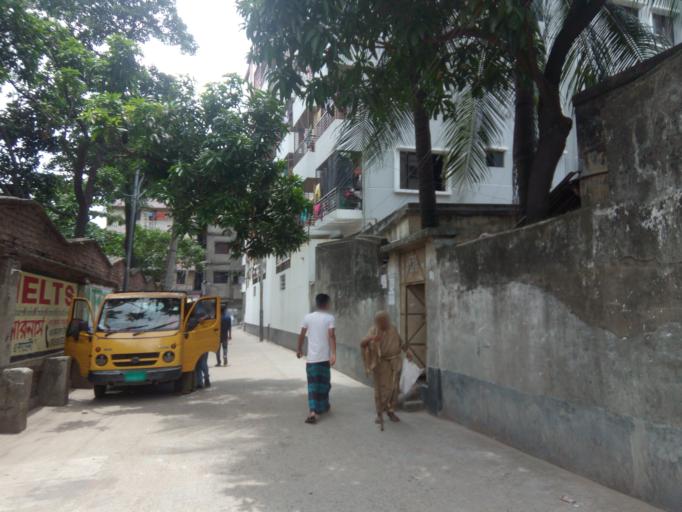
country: BD
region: Dhaka
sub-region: Dhaka
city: Dhaka
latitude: 23.7154
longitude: 90.4248
